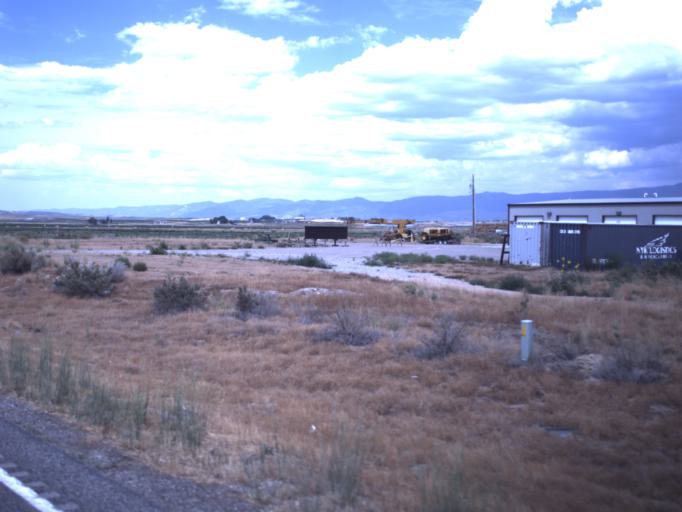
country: US
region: Utah
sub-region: Sanpete County
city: Moroni
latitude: 39.4604
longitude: -111.5626
